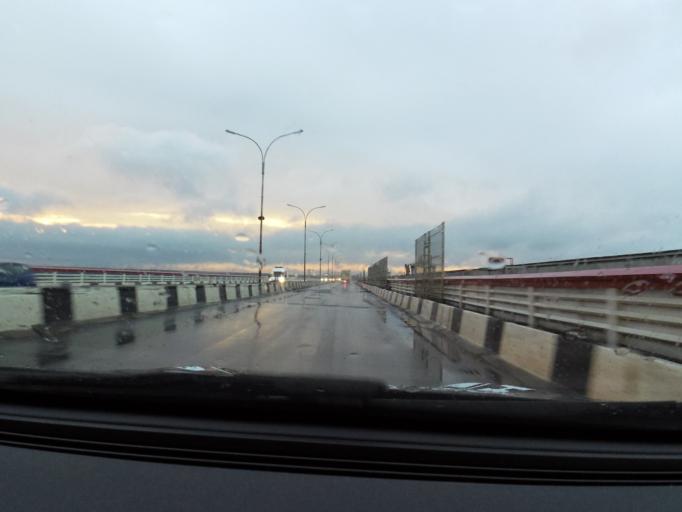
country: RU
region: Tatarstan
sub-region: Tukayevskiy Rayon
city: Naberezhnyye Chelny
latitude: 55.6971
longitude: 52.2794
